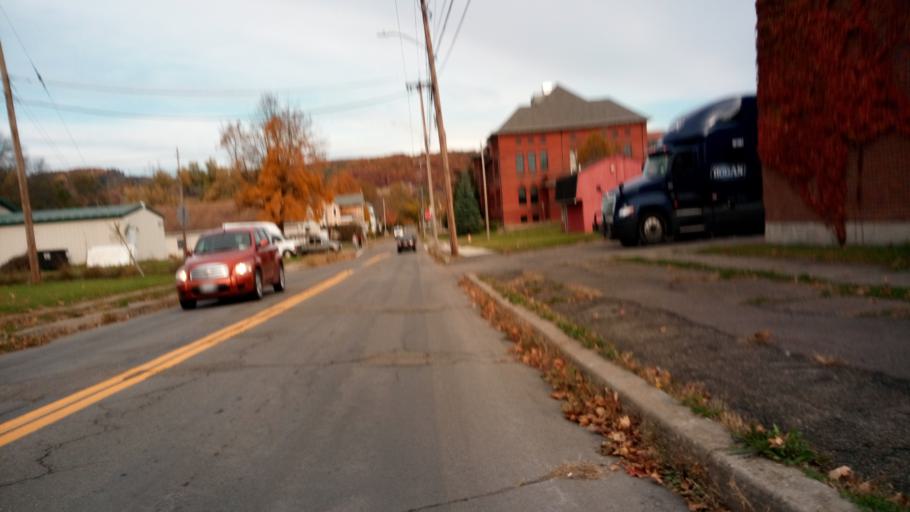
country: US
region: New York
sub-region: Chemung County
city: Elmira
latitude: 42.0934
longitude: -76.8015
